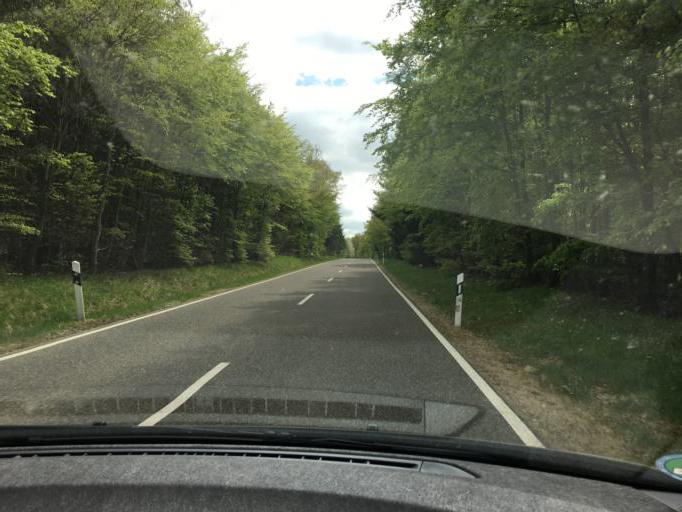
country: DE
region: North Rhine-Westphalia
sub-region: Regierungsbezirk Koln
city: Bad Munstereifel
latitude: 50.5410
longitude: 6.8201
